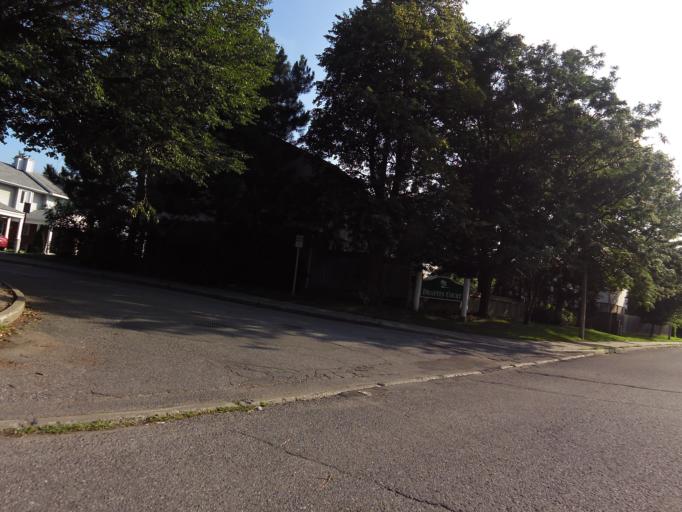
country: CA
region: Ontario
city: Bells Corners
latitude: 45.3453
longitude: -75.7700
